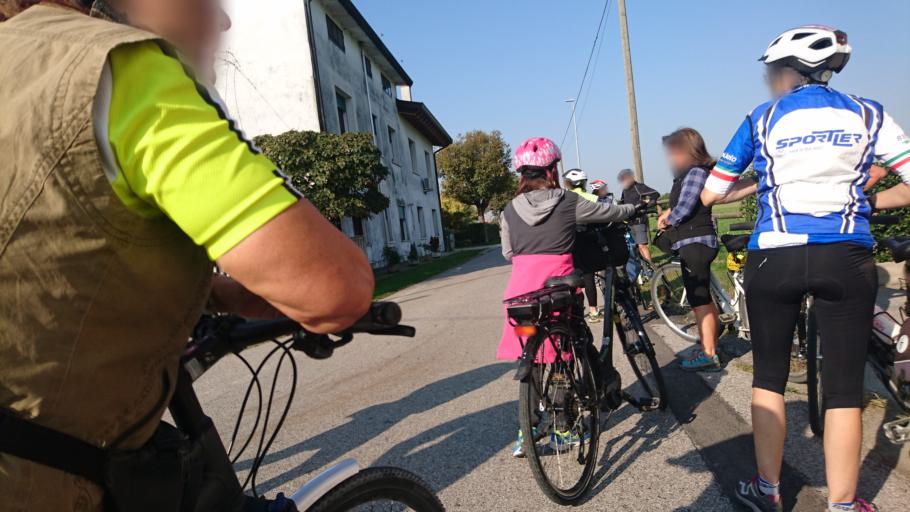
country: IT
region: Veneto
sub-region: Provincia di Padova
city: Gazzo
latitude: 45.6017
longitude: 11.7096
